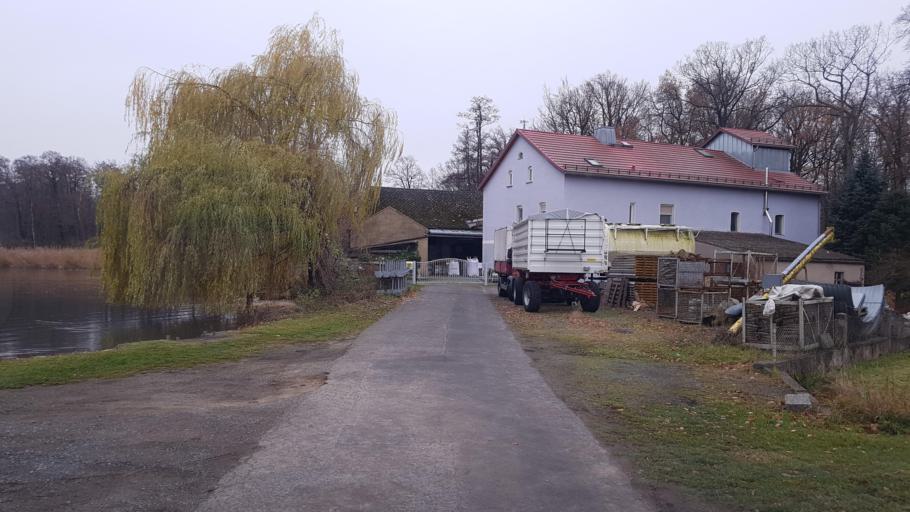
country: DE
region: Brandenburg
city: Lindenau
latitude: 51.3991
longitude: 13.7197
